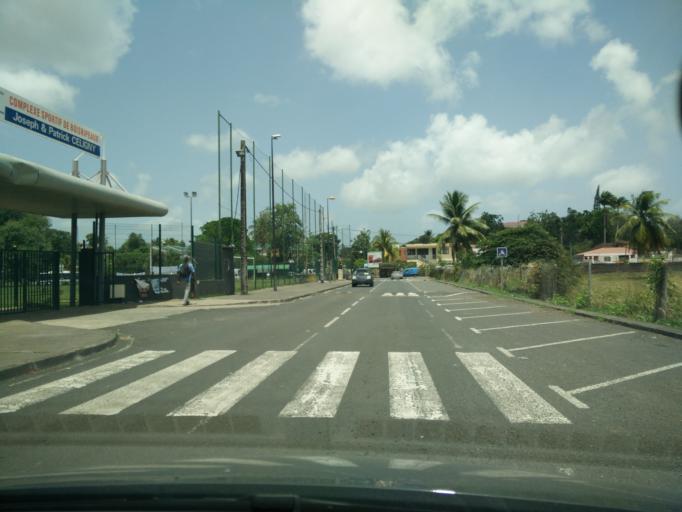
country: GP
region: Guadeloupe
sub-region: Guadeloupe
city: Les Abymes
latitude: 16.2769
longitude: -61.5022
